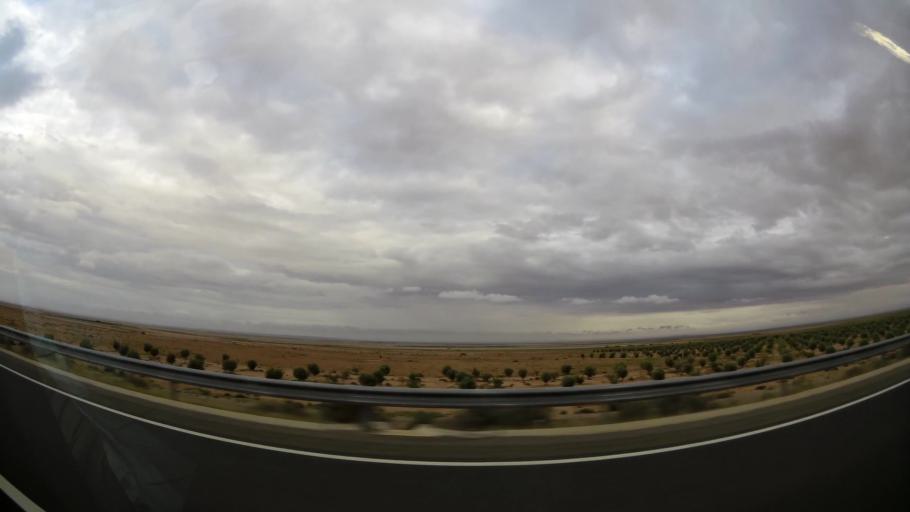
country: MA
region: Taza-Al Hoceima-Taounate
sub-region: Taza
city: Guercif
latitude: 34.3251
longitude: -3.5650
